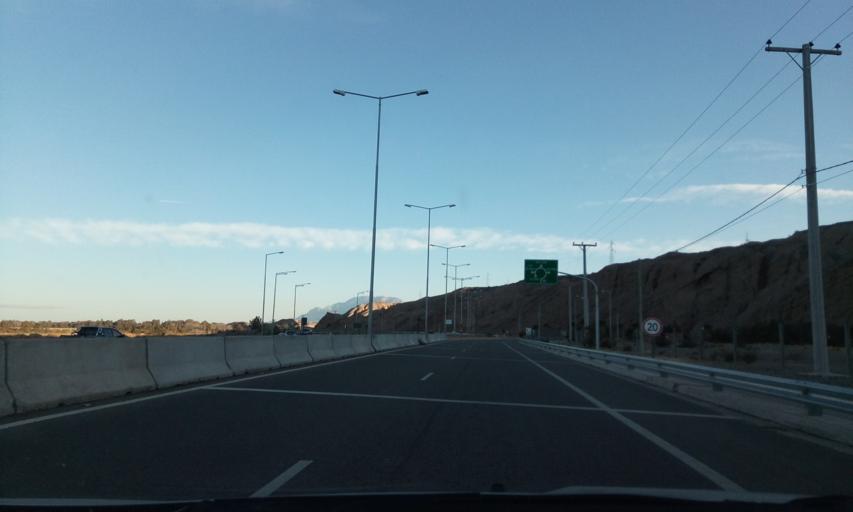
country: AR
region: San Juan
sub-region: Departamento de Rivadavia
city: Rivadavia
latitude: -31.4868
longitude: -68.6488
